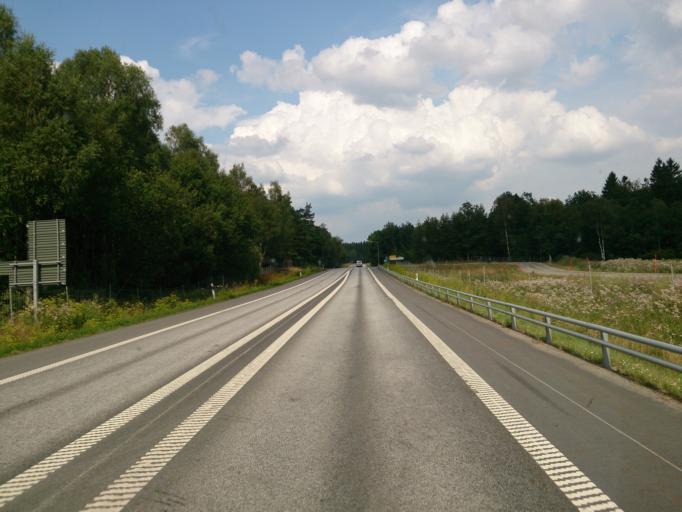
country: SE
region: Skane
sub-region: Horby Kommun
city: Hoerby
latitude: 55.9236
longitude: 13.7913
